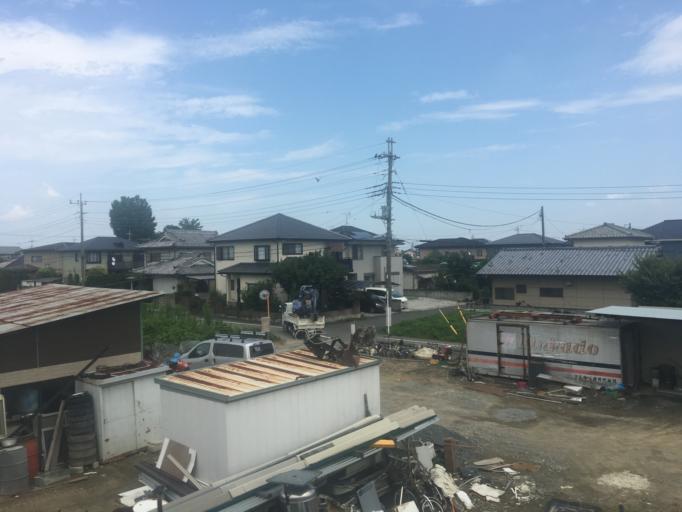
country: JP
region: Gunma
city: Fujioka
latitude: 36.2776
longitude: 139.0839
